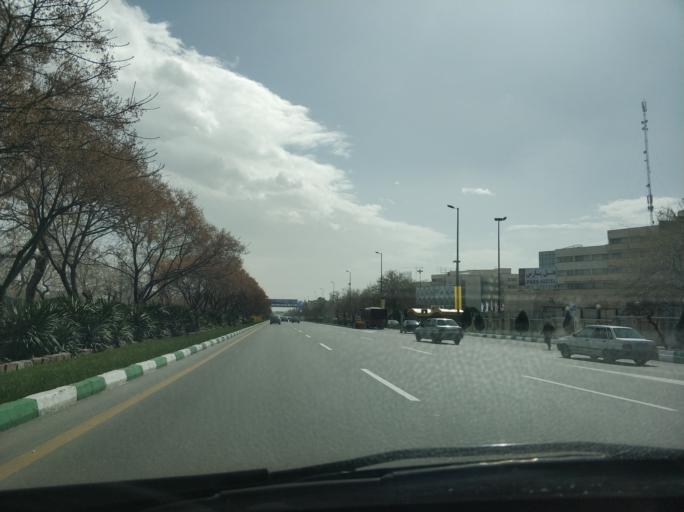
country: IR
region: Razavi Khorasan
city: Mashhad
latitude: 36.3320
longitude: 59.4859
